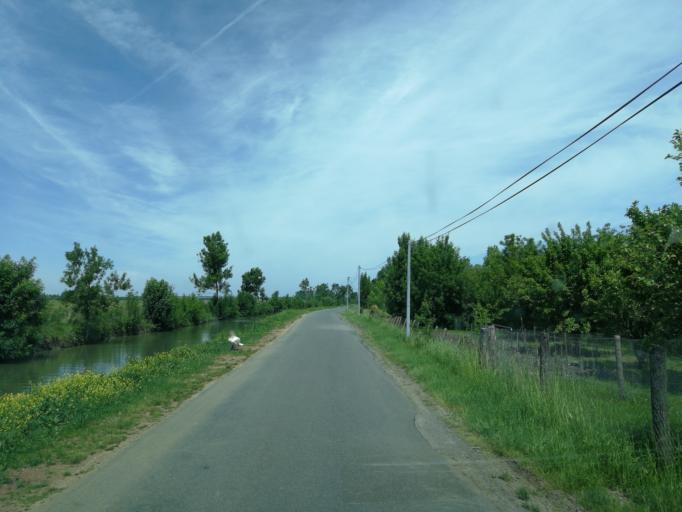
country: FR
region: Pays de la Loire
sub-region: Departement de la Vendee
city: Le Langon
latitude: 46.4067
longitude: -0.9249
